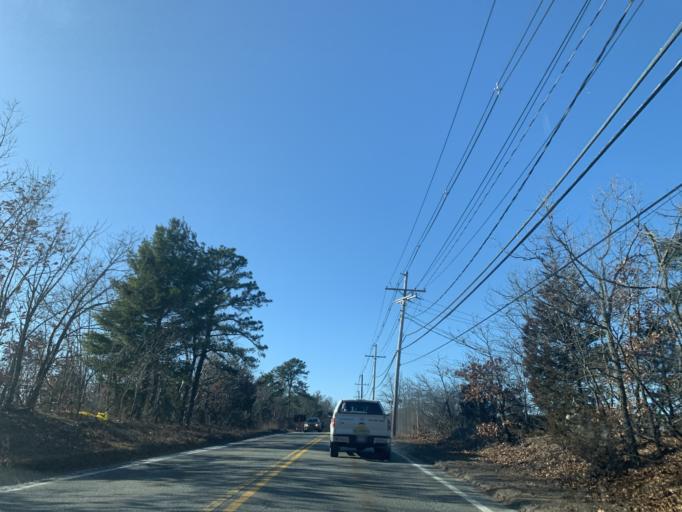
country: US
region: Massachusetts
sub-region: Middlesex County
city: Wayland
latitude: 42.3630
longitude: -71.3842
